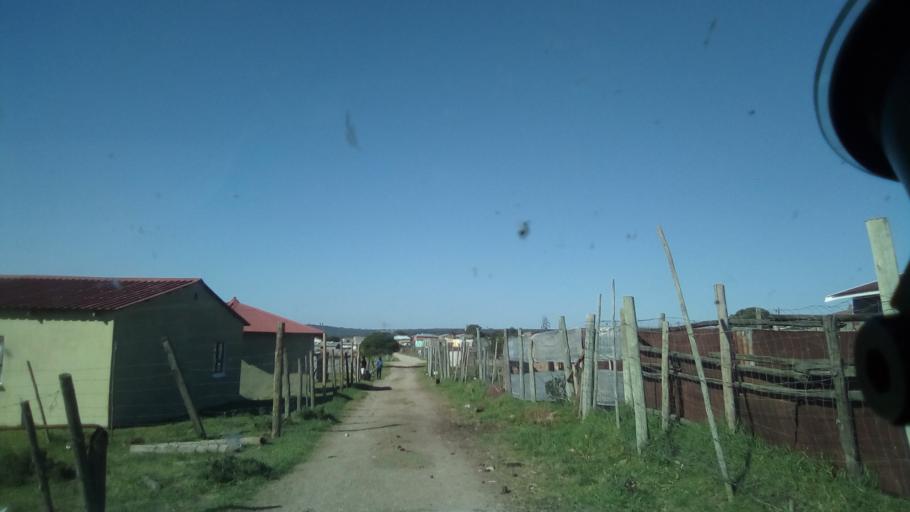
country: ZA
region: Eastern Cape
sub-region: Buffalo City Metropolitan Municipality
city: Bhisho
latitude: -32.8304
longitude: 27.3680
